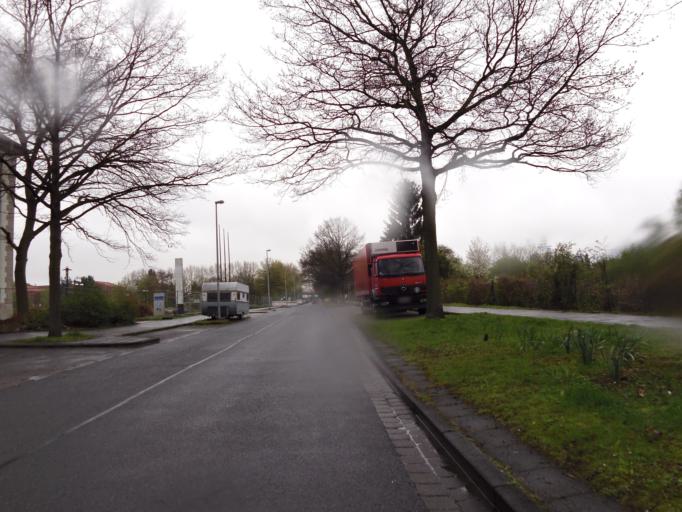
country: DE
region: Lower Saxony
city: Laatzen
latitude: 52.3779
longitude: 9.7981
